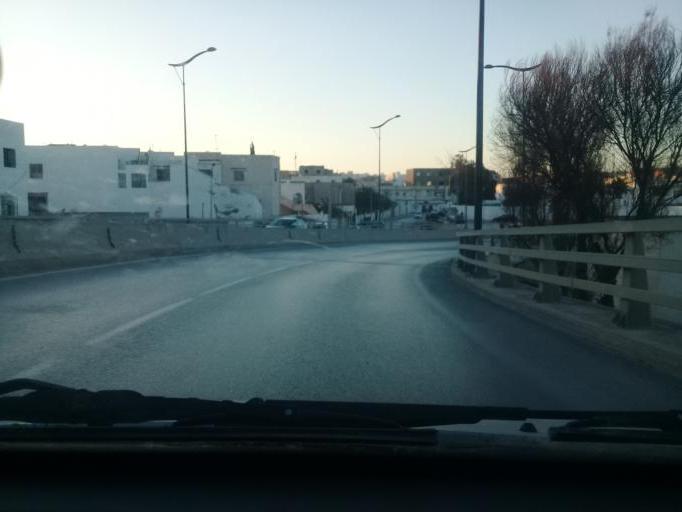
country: TN
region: Tunis
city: La Goulette
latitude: 36.8531
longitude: 10.2723
